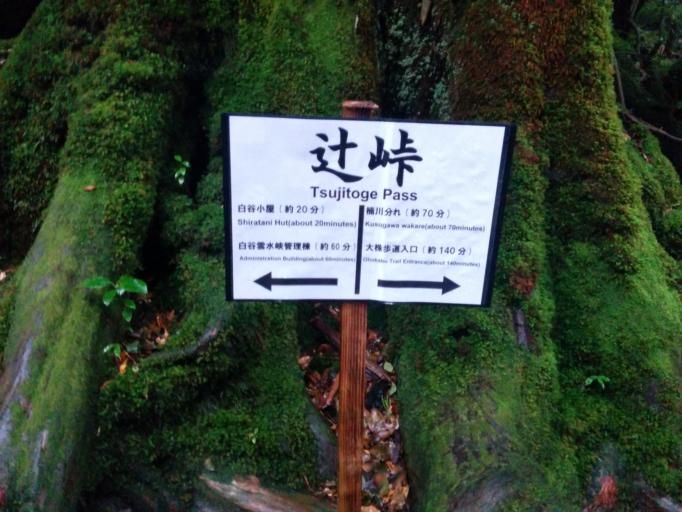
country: JP
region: Kagoshima
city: Nishinoomote
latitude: 30.3640
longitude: 130.5675
